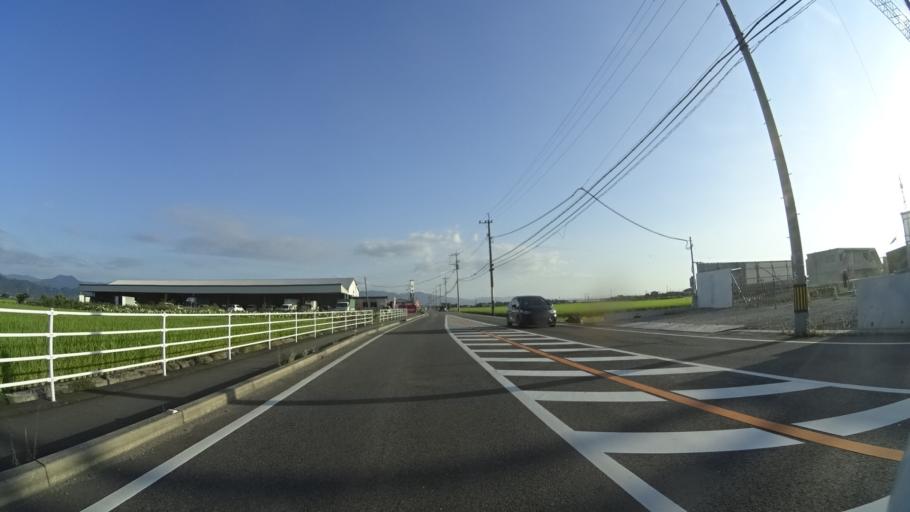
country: JP
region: Kumamoto
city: Matsubase
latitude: 32.6380
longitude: 130.6753
